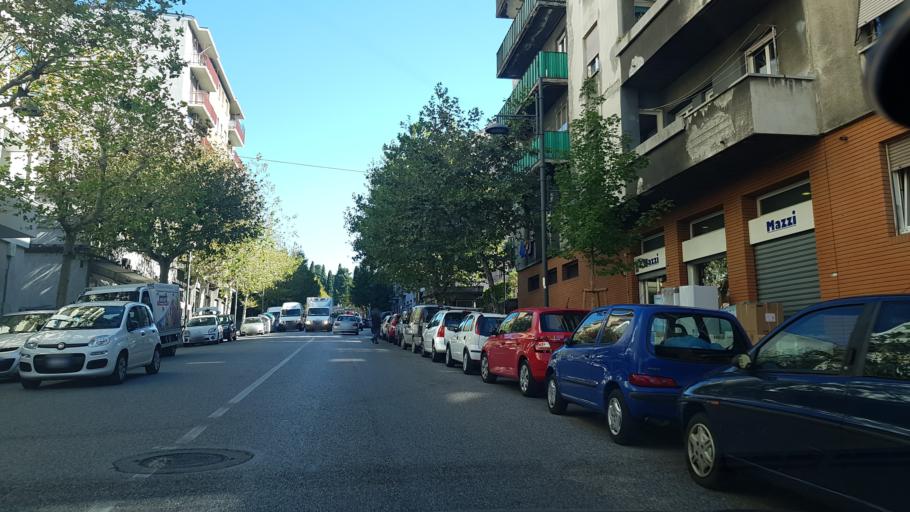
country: IT
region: Friuli Venezia Giulia
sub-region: Provincia di Trieste
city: Trieste
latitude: 45.6305
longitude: 13.7892
